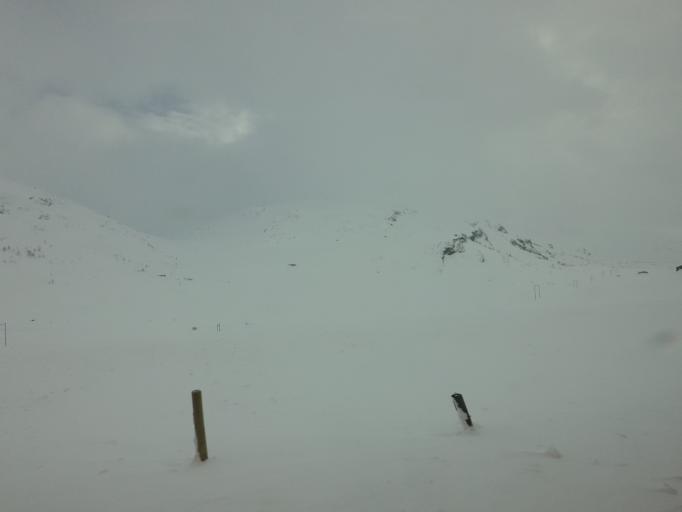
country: NO
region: Hordaland
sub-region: Ulvik
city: Ulvik
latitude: 60.7254
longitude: 7.0123
